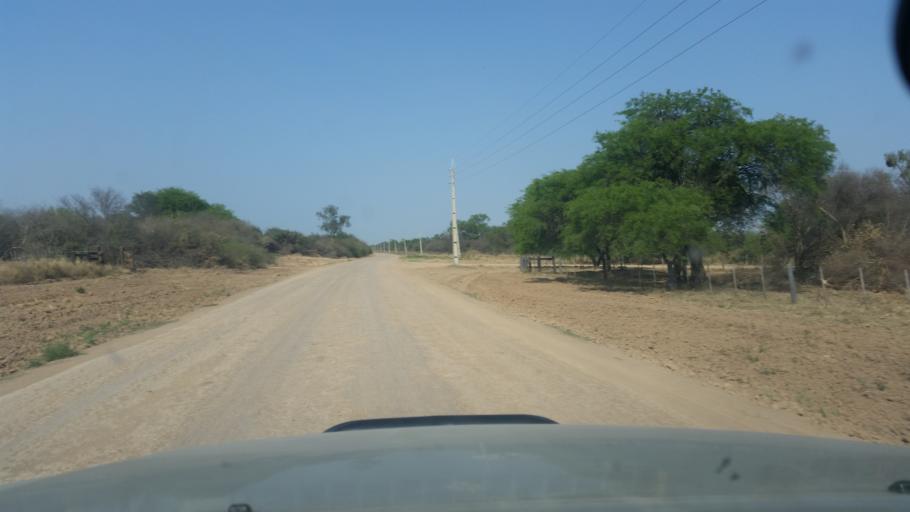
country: PY
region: Boqueron
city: Filadelfia
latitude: -22.0780
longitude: -60.6654
